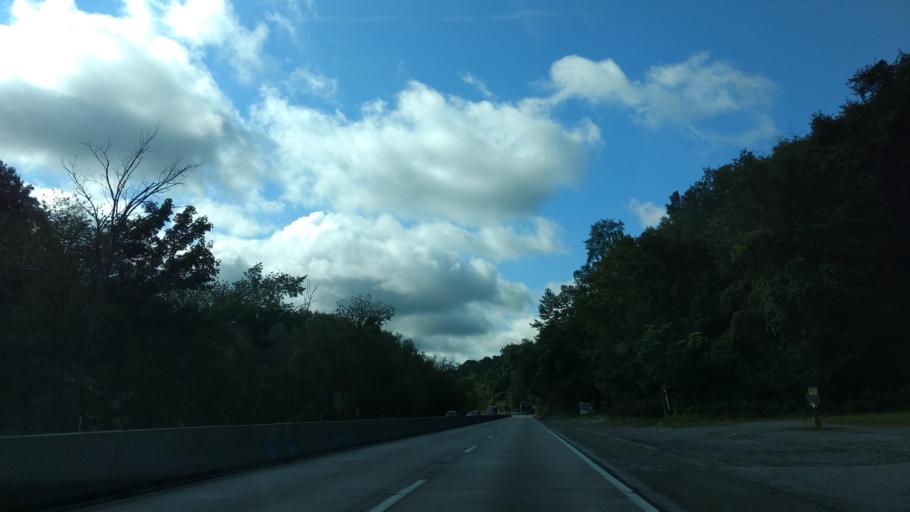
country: US
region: Pennsylvania
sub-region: Allegheny County
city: Elizabeth
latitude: 40.2589
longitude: -79.8789
